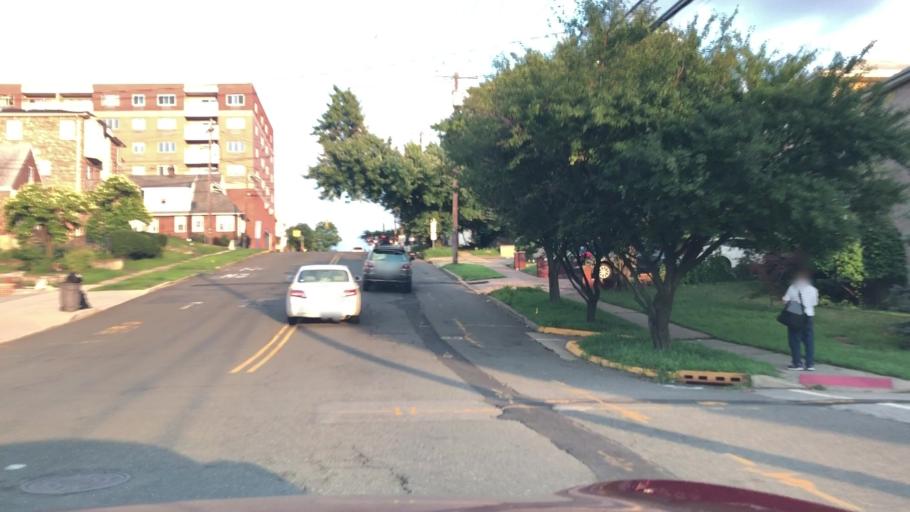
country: US
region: New Jersey
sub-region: Bergen County
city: Palisades Park
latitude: 40.8420
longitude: -73.9900
